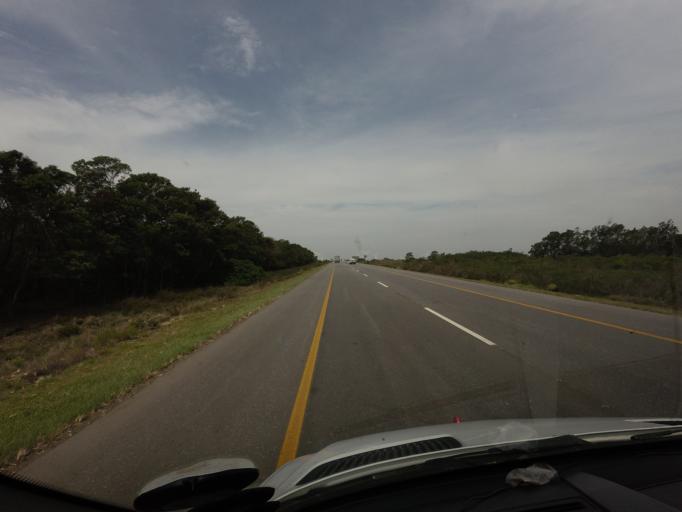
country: ZA
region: Eastern Cape
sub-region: Cacadu District Municipality
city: Kruisfontein
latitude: -34.0096
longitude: 24.7898
